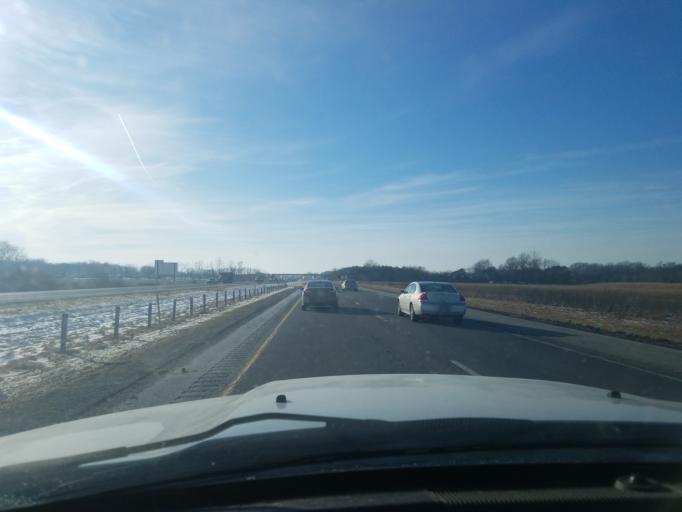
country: US
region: Indiana
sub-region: Madison County
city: Anderson
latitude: 40.0511
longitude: -85.6708
